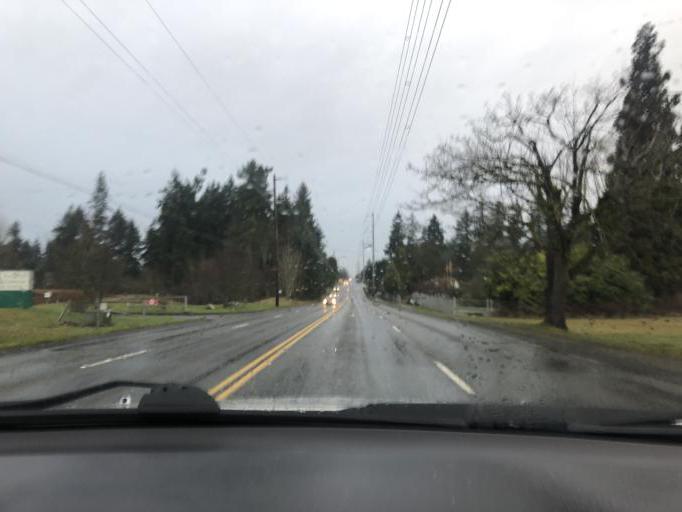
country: US
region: Washington
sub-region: Pierce County
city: Waller
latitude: 47.1918
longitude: -122.3922
